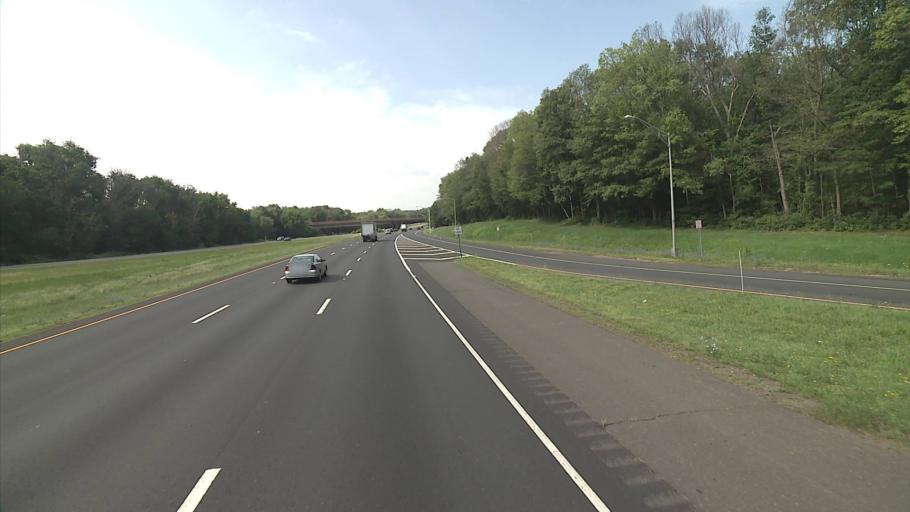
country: US
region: Connecticut
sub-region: New Haven County
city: Wallingford Center
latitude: 41.4574
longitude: -72.7793
